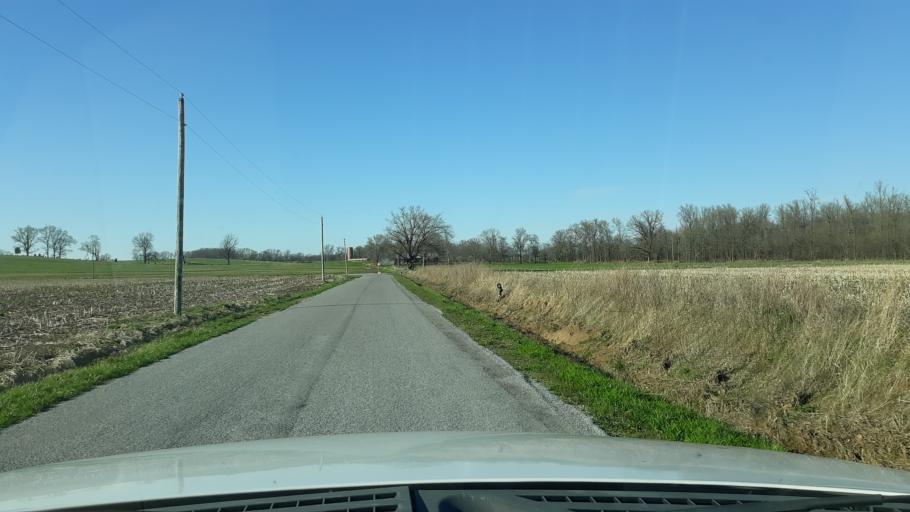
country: US
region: Illinois
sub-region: Saline County
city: Harrisburg
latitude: 37.7740
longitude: -88.5863
